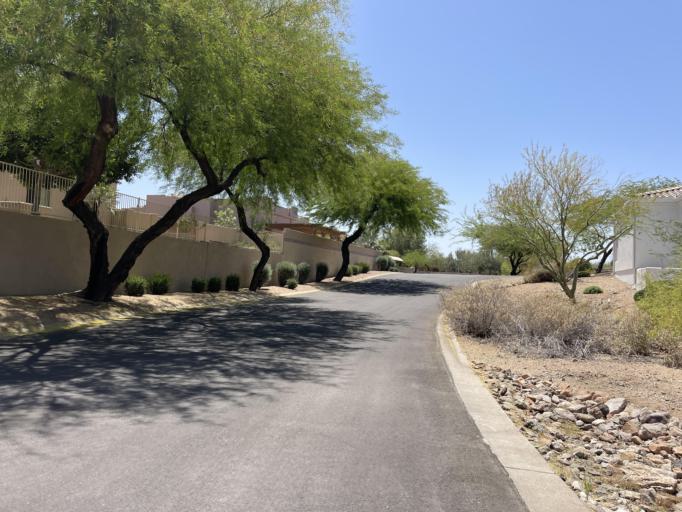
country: US
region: Arizona
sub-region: Maricopa County
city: Fountain Hills
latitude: 33.4902
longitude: -111.6907
